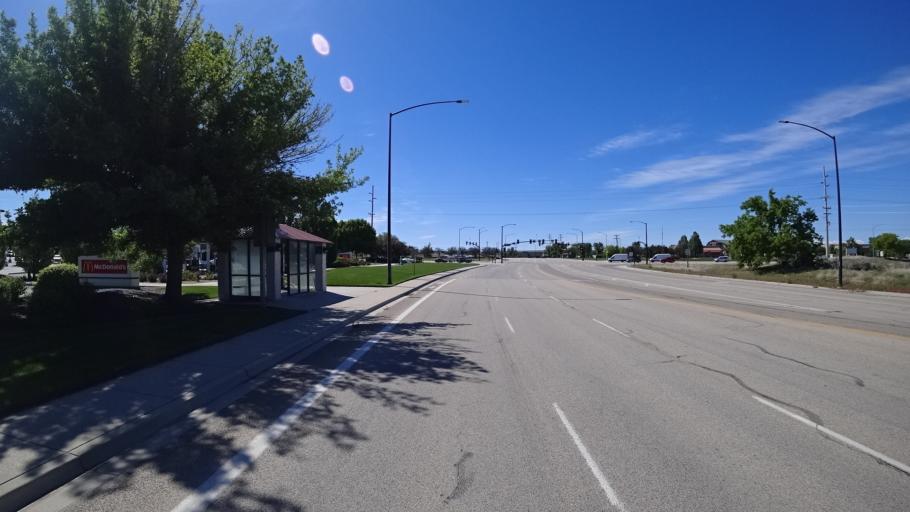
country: US
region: Idaho
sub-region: Ada County
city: Boise
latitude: 43.5420
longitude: -116.1554
